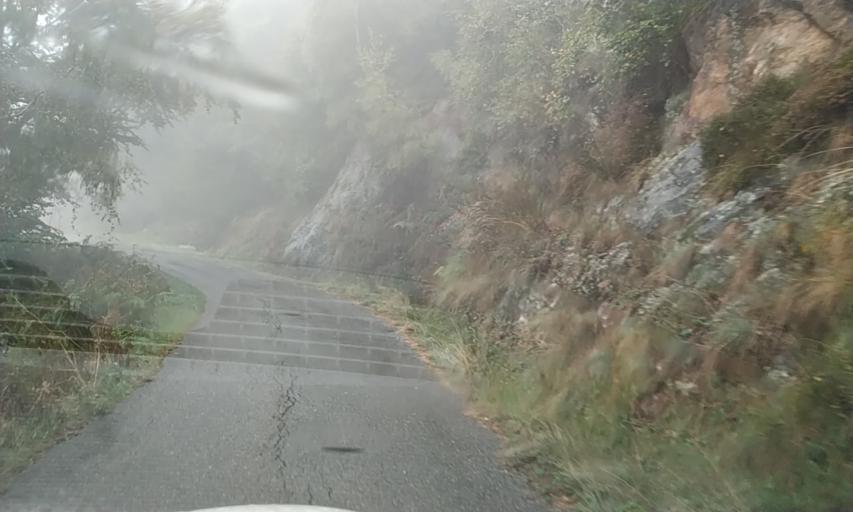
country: IT
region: Piedmont
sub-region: Provincia Verbano-Cusio-Ossola
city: Cesara
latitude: 45.8414
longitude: 8.3240
